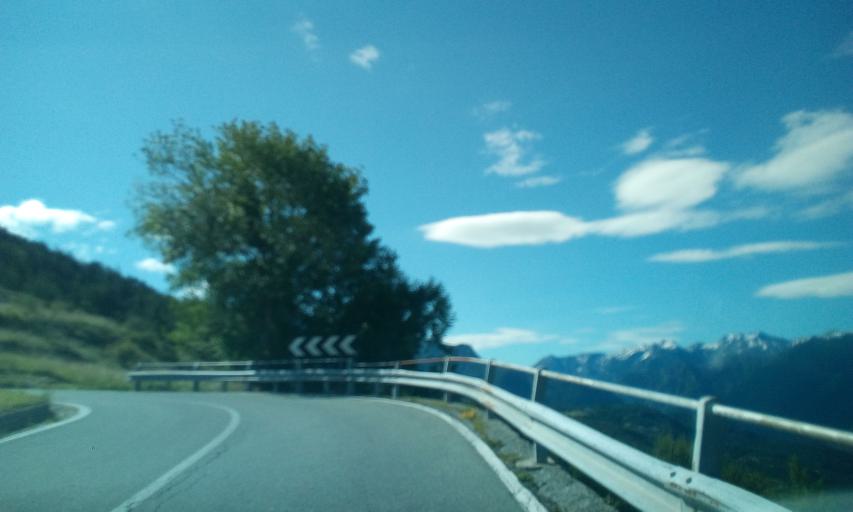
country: IT
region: Aosta Valley
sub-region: Valle d'Aosta
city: Emarese
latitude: 45.7399
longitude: 7.6817
